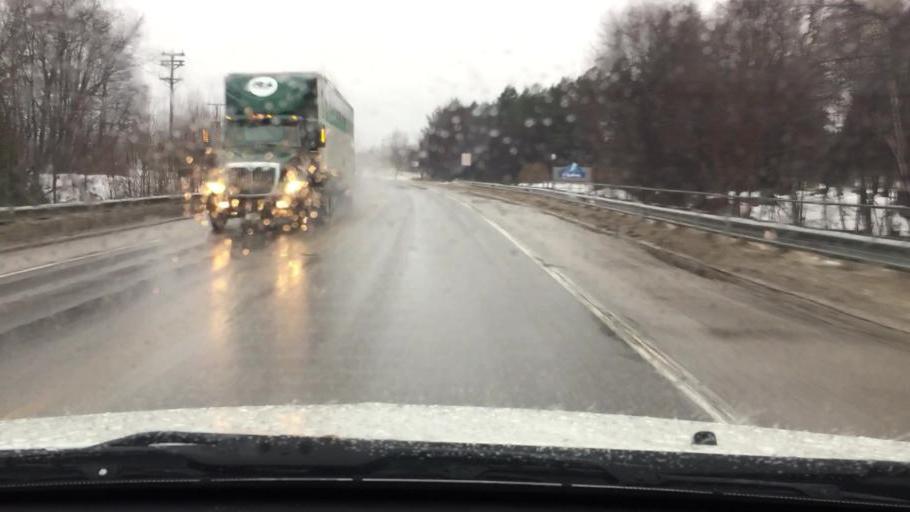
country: US
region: Michigan
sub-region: Charlevoix County
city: Charlevoix
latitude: 45.3005
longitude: -85.2569
